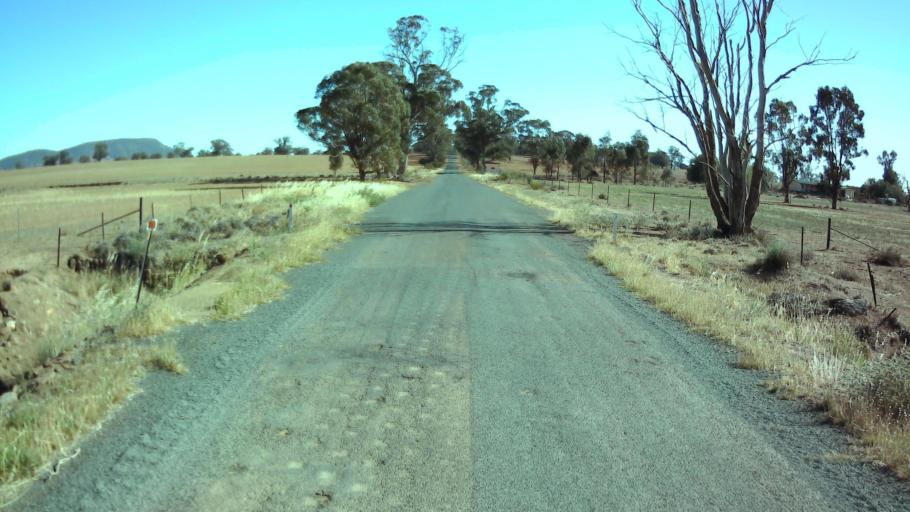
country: AU
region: New South Wales
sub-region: Weddin
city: Grenfell
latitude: -33.7931
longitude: 147.9571
